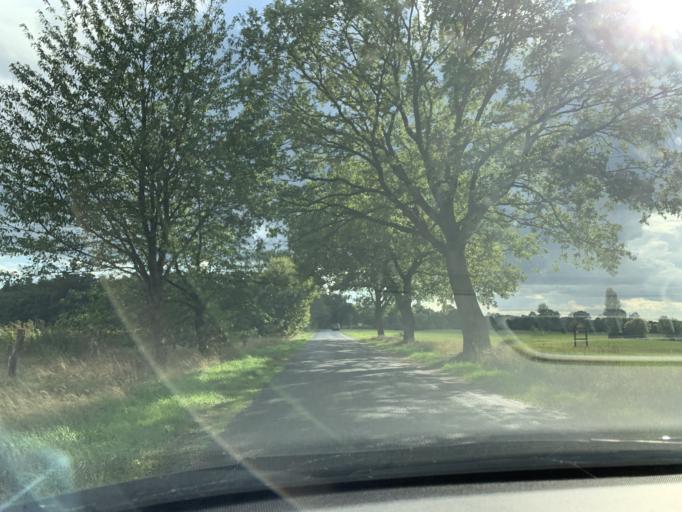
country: DE
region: Lower Saxony
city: Westerstede
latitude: 53.3114
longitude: 7.9759
